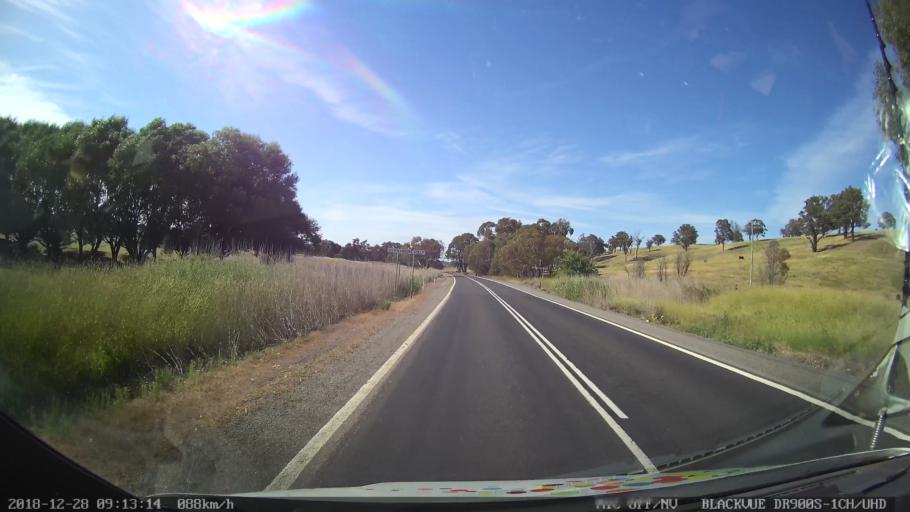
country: AU
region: New South Wales
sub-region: Upper Lachlan Shire
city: Crookwell
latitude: -34.2663
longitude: 149.3429
